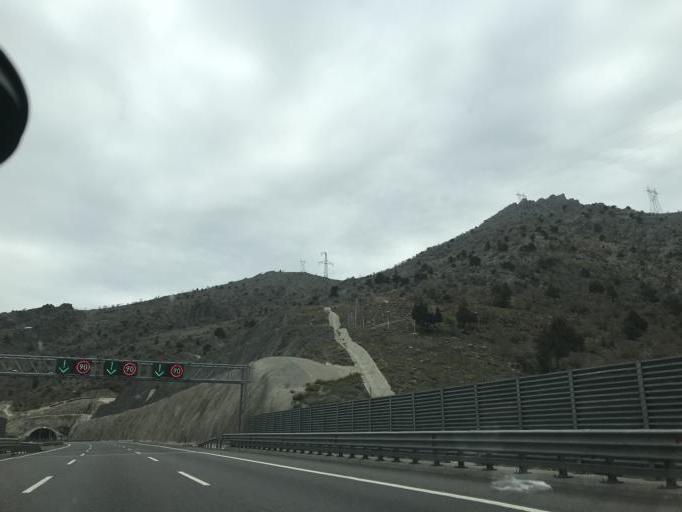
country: TR
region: Nigde
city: Ciftehan
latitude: 37.5467
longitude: 34.7842
